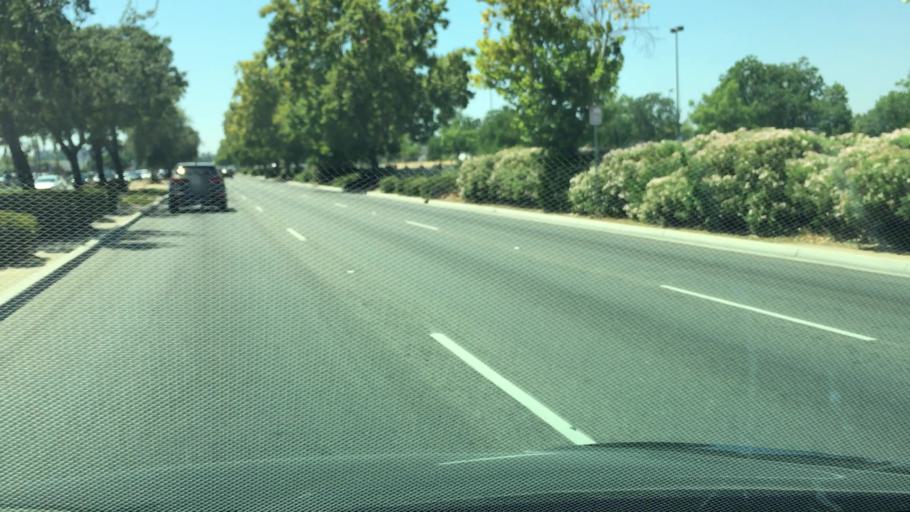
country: US
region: California
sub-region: Fresno County
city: Fresno
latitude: 36.8371
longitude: -119.8037
